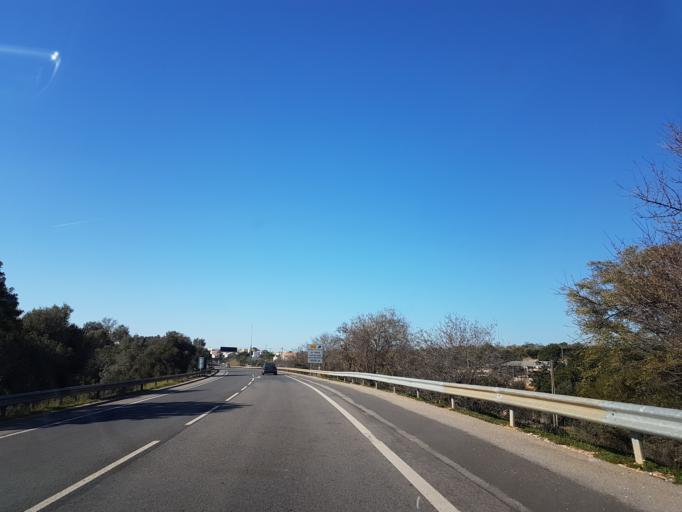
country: PT
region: Faro
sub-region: Portimao
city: Portimao
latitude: 37.1585
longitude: -8.5443
